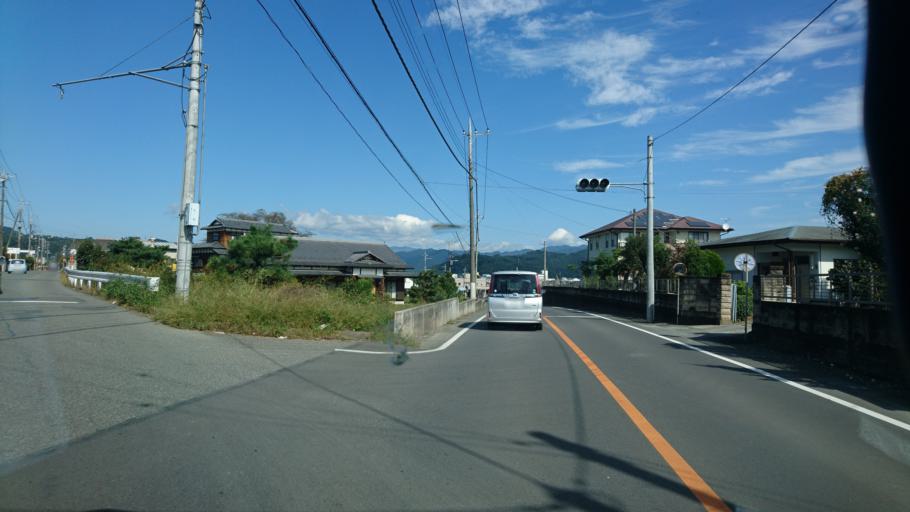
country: JP
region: Gunma
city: Omamacho-omama
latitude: 36.4207
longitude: 139.2704
